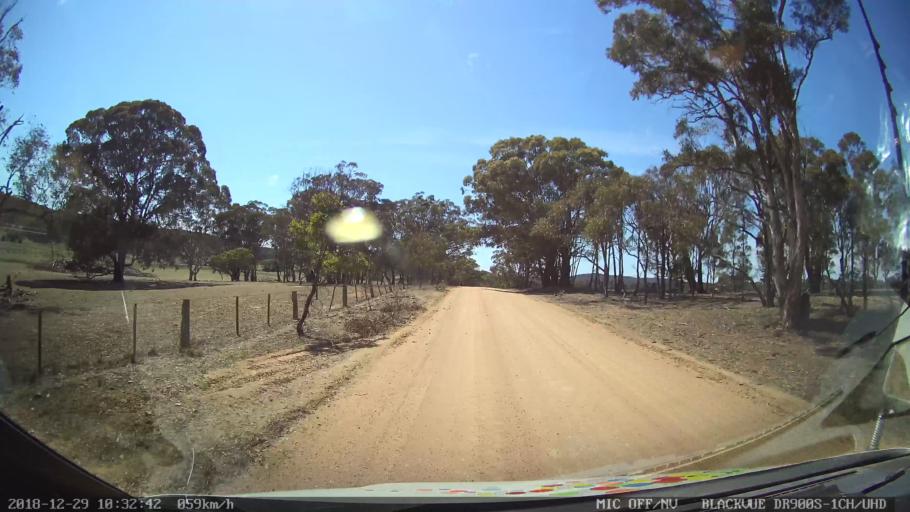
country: AU
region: New South Wales
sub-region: Yass Valley
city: Gundaroo
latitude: -34.9760
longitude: 149.4672
